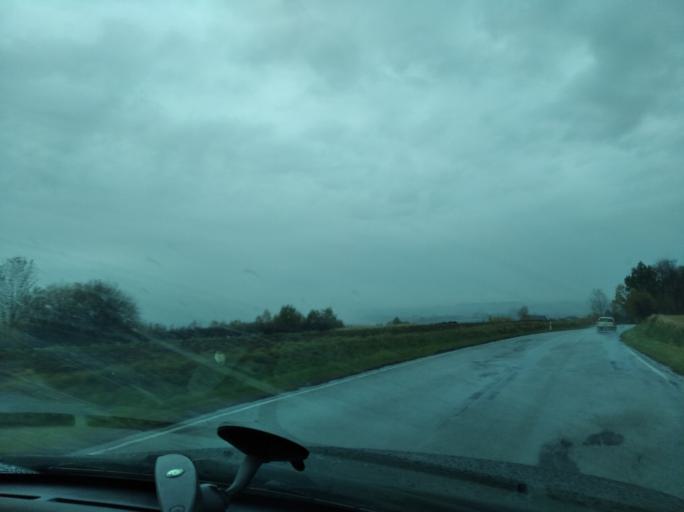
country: PL
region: Subcarpathian Voivodeship
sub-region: Powiat lancucki
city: Handzlowka
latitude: 50.0021
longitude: 22.2020
